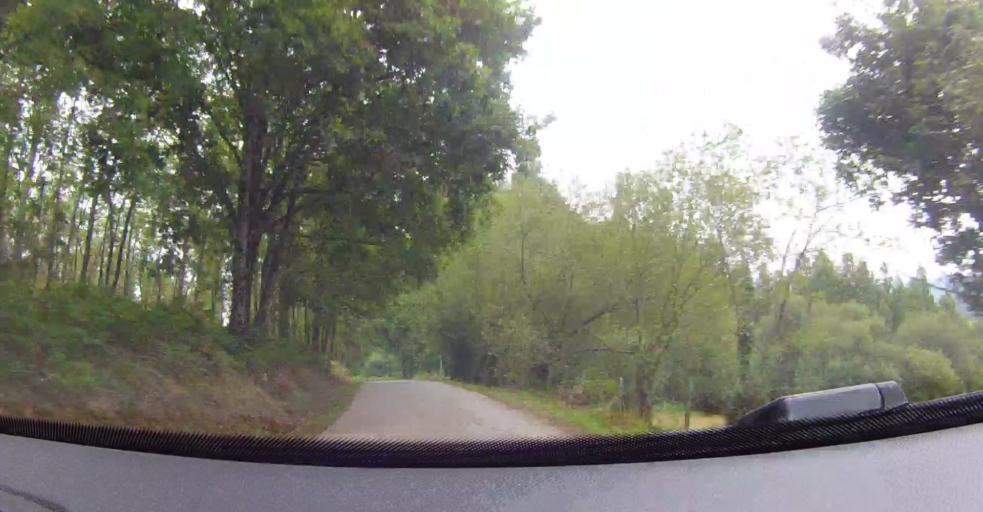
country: ES
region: Basque Country
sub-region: Bizkaia
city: Urrestieta
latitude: 43.2306
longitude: -3.1772
